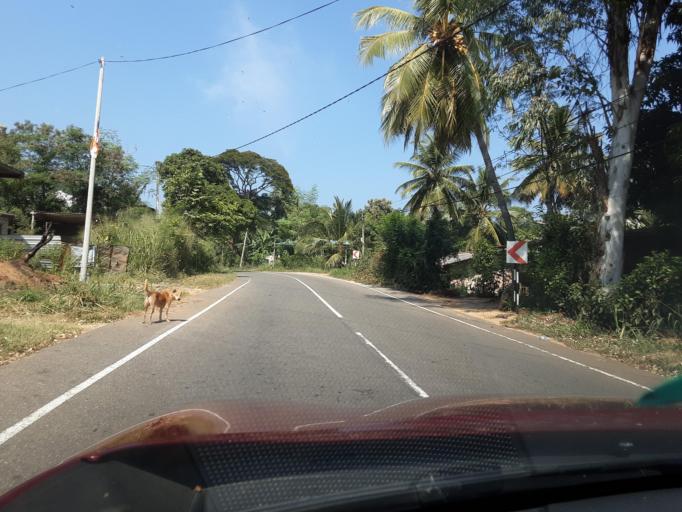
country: LK
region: Uva
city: Badulla
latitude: 7.1835
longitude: 81.0448
